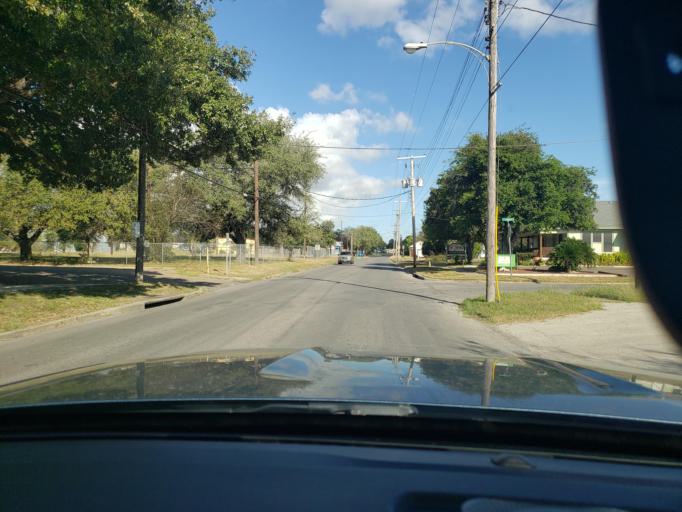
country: US
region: Texas
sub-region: Bee County
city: Beeville
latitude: 28.4088
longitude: -97.7519
